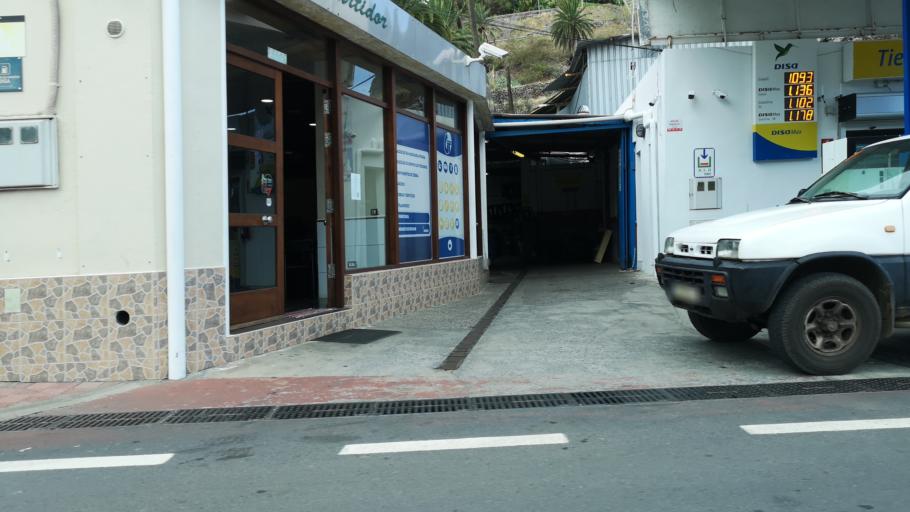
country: ES
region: Canary Islands
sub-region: Provincia de Santa Cruz de Tenerife
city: Hermigua
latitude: 28.1722
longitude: -17.1886
